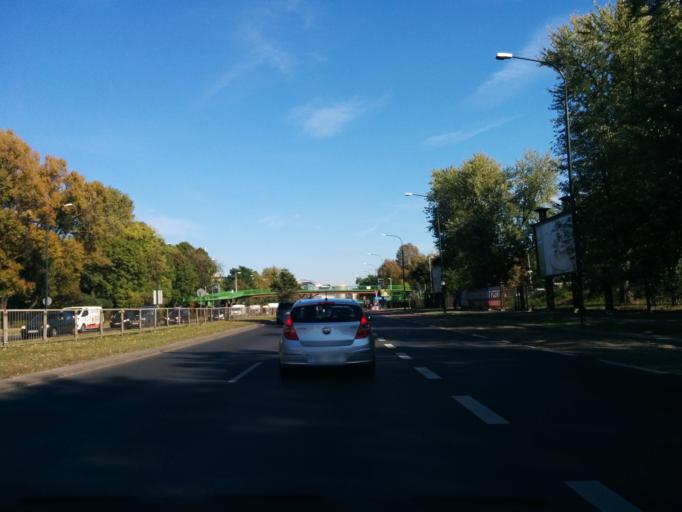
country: PL
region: Masovian Voivodeship
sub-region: Warszawa
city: Ochota
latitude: 52.2164
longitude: 20.9923
